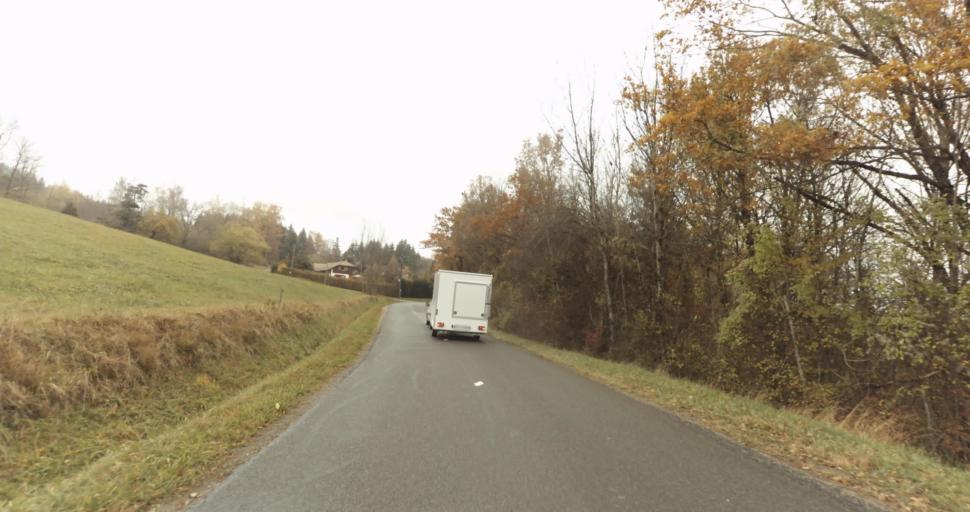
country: FR
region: Rhone-Alpes
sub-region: Departement de la Haute-Savoie
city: Groisy
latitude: 46.0223
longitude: 6.1789
